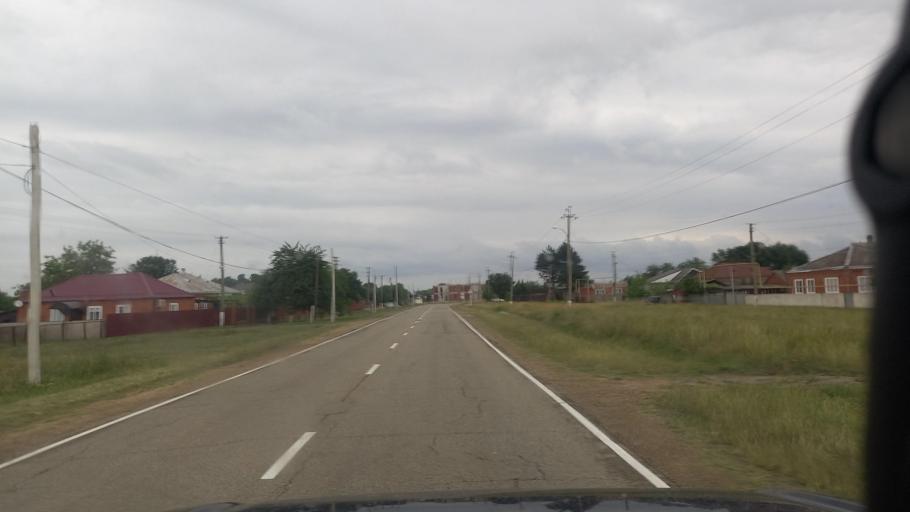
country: RU
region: Adygeya
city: Adygeysk
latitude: 44.8826
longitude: 39.2376
